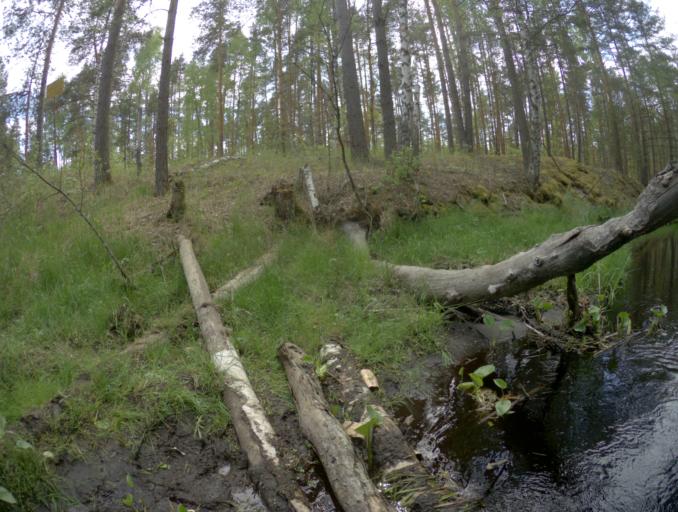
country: RU
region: Vladimir
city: Ivanishchi
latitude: 55.6969
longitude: 40.4274
